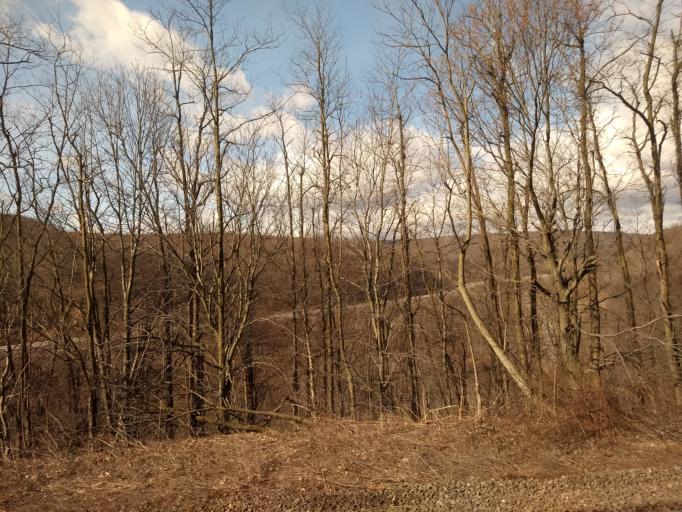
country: US
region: Pennsylvania
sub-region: Cambria County
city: Gallitzin
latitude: 40.4774
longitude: -78.4933
